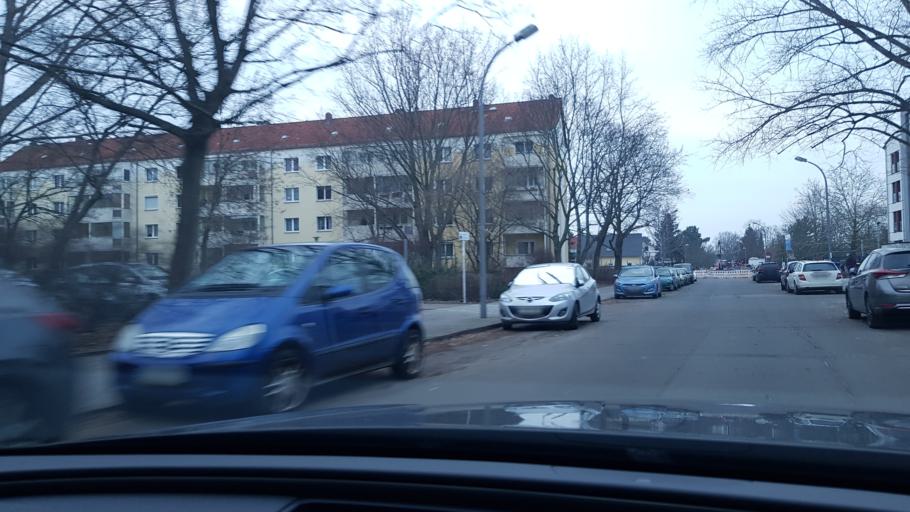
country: DE
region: Berlin
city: Grunau
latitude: 52.4279
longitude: 13.5929
